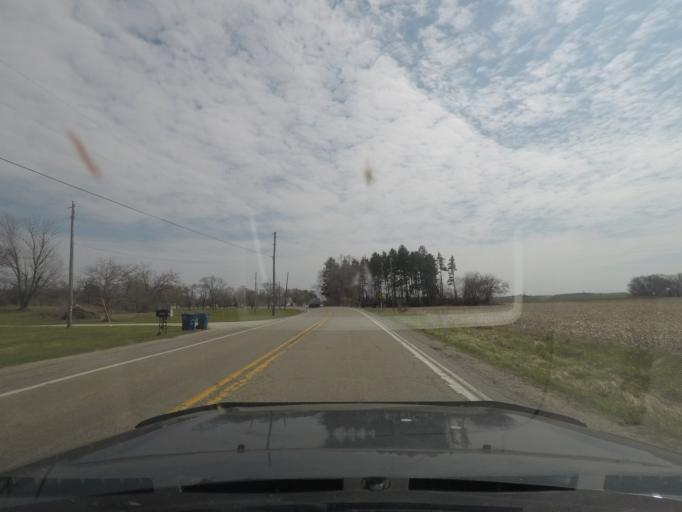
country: US
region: Indiana
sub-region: LaPorte County
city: Kingsford Heights
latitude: 41.4782
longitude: -86.6781
